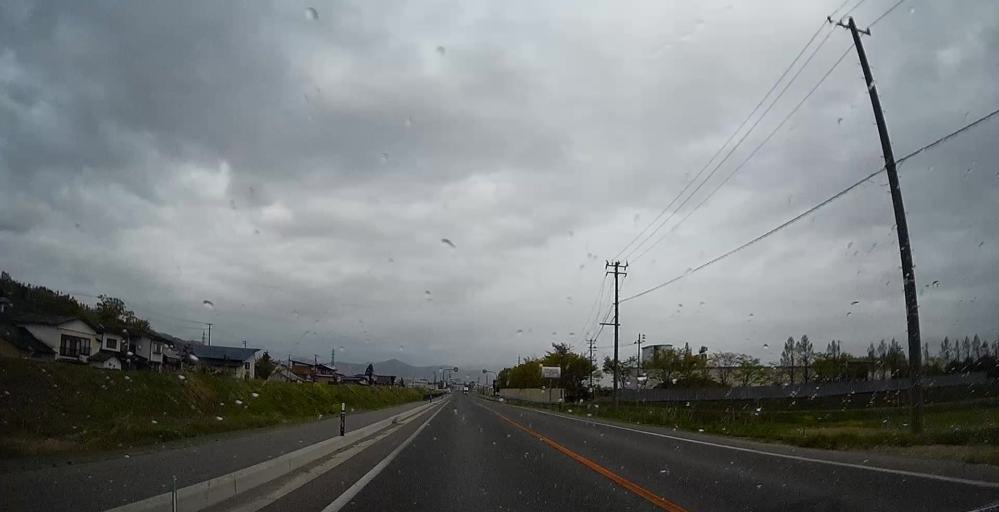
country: JP
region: Yamagata
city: Nagai
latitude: 38.0518
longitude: 140.0872
